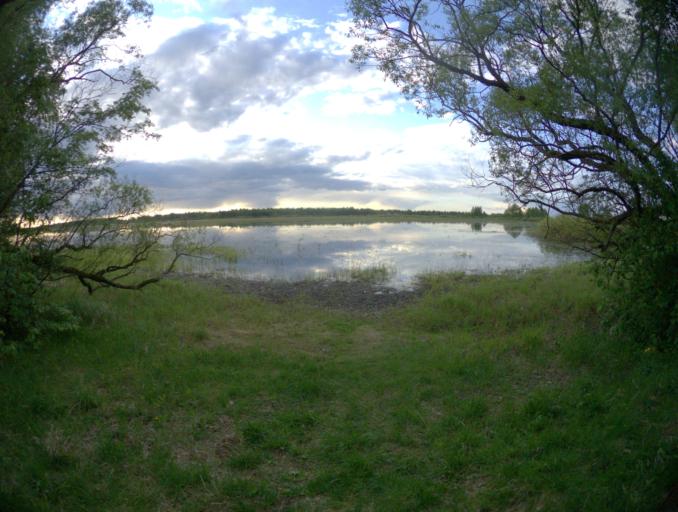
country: RU
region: Rjazan
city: Spas-Klepiki
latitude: 55.2550
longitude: 40.1133
